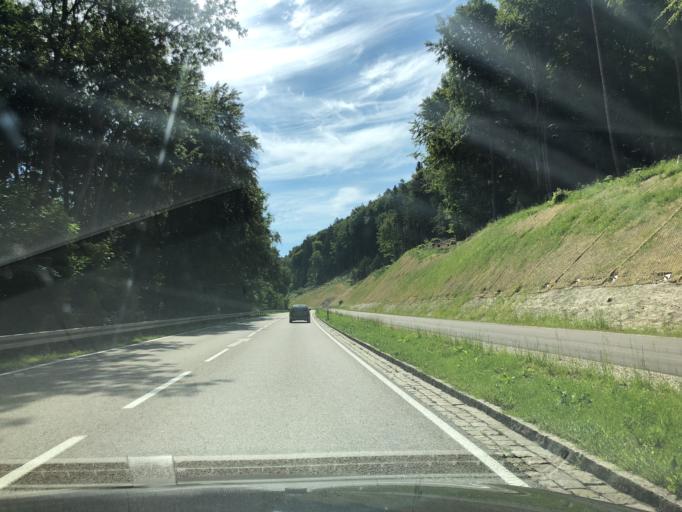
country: DE
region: Bavaria
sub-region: Upper Bavaria
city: Denkendorf
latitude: 49.0182
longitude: 11.4834
